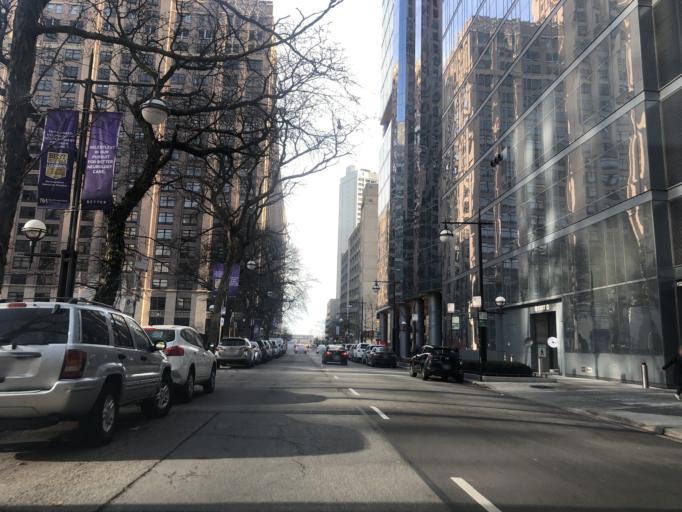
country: US
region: Illinois
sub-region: Cook County
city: Chicago
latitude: 41.8943
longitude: -87.6191
